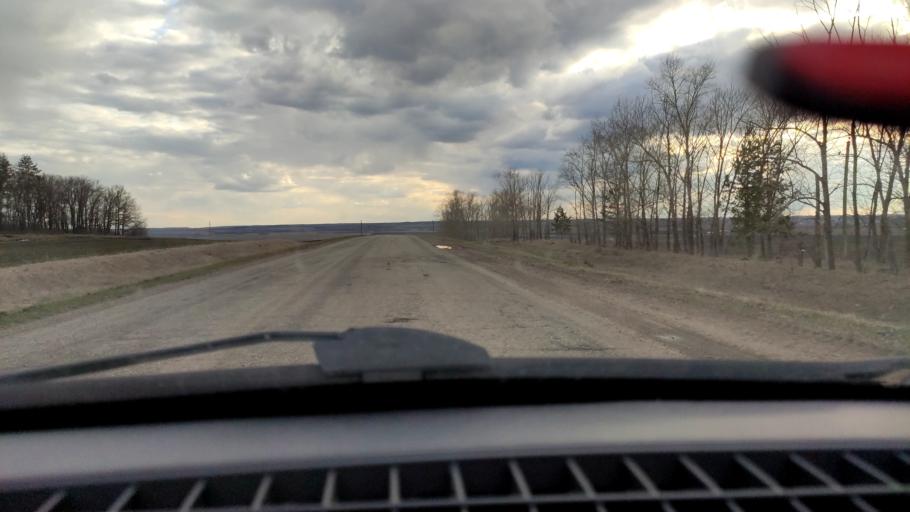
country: RU
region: Bashkortostan
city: Karmaskaly
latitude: 54.3004
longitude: 55.9254
